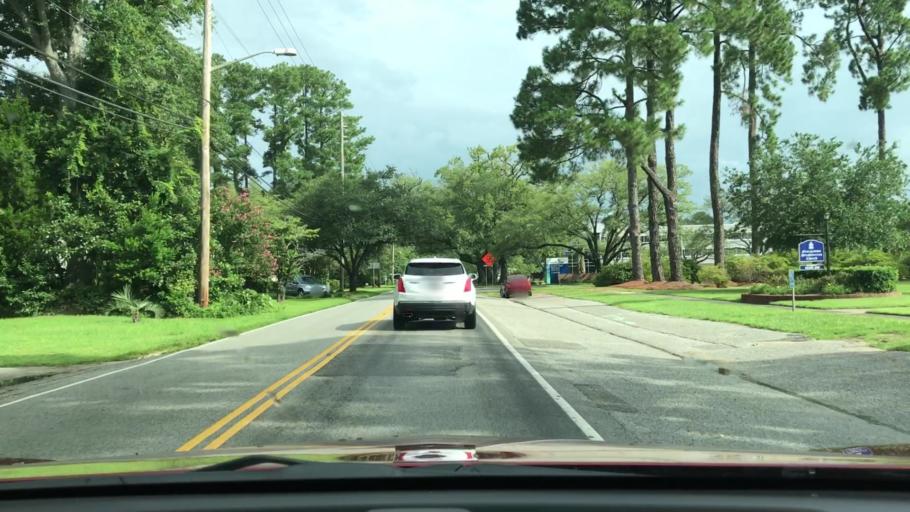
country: US
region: South Carolina
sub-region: Georgetown County
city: Georgetown
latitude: 33.3775
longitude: -79.2846
